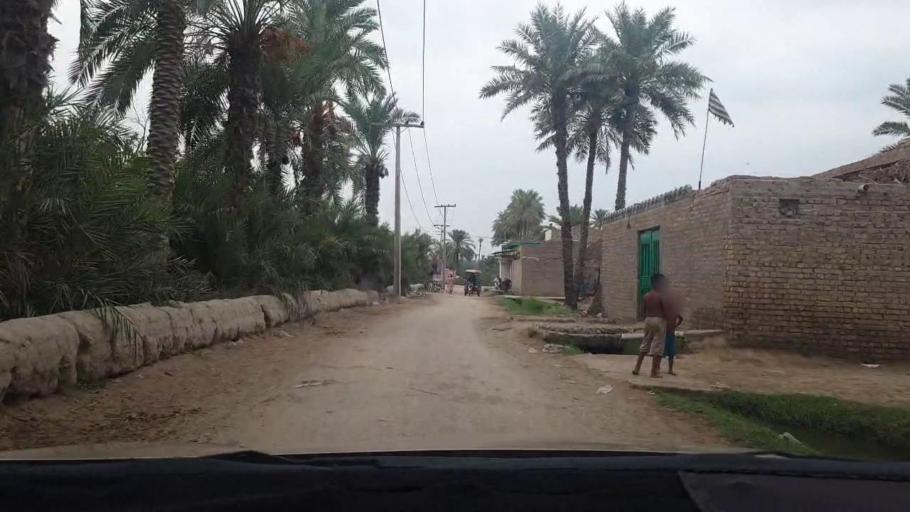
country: PK
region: Sindh
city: Larkana
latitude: 27.5654
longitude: 68.2297
